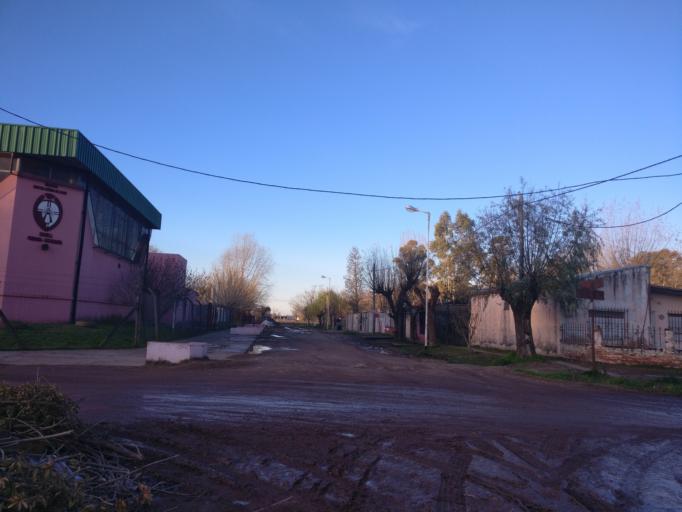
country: AR
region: Buenos Aires
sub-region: Partido de Ezeiza
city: Ezeiza
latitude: -34.9377
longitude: -58.6160
